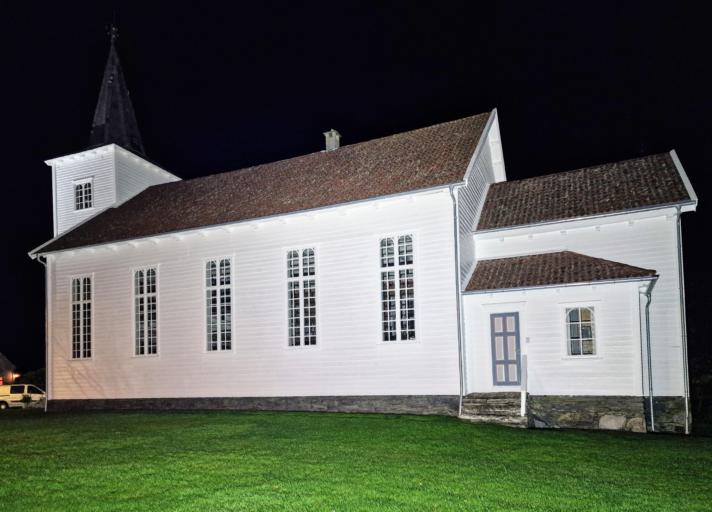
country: NO
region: Rogaland
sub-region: Finnoy
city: Judaberg
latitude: 59.3496
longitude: 5.8008
